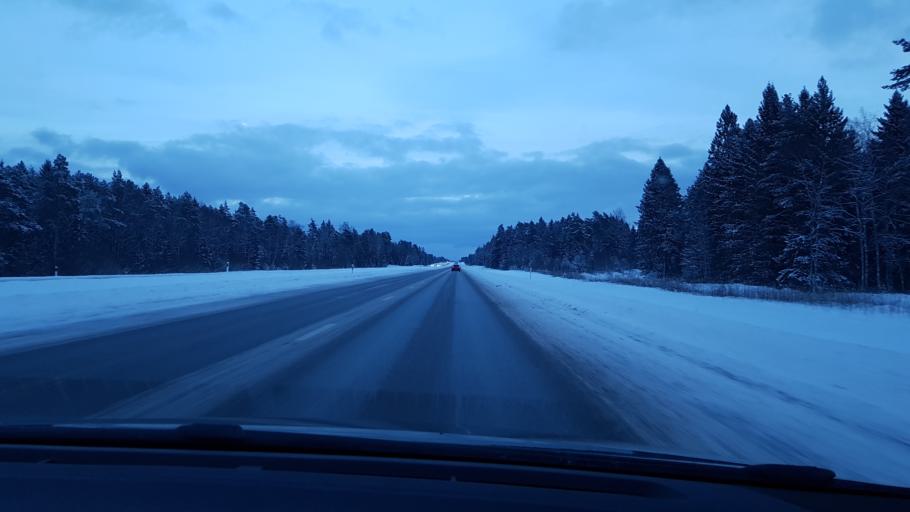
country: EE
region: Harju
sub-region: Raasiku vald
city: Raasiku
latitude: 59.4369
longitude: 25.2304
